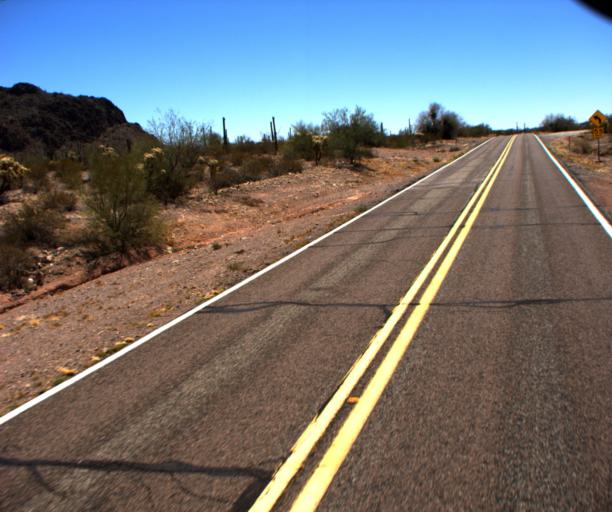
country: US
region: Arizona
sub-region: Pima County
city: Ajo
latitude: 32.2236
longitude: -112.7002
